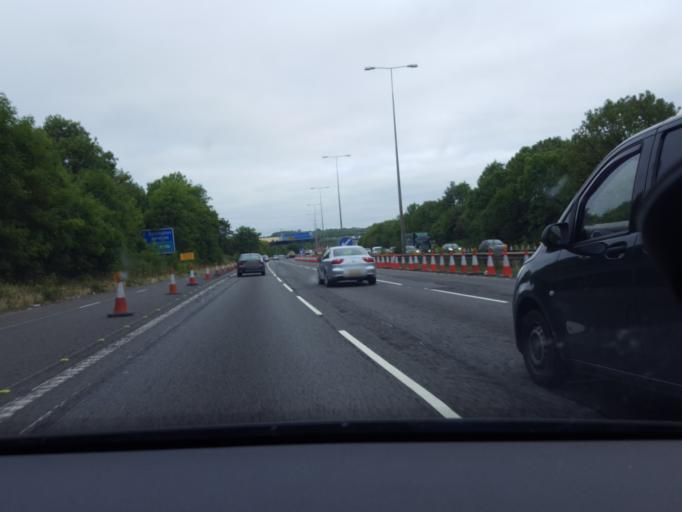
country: GB
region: England
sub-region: Leicestershire
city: Kegworth
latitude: 52.8065
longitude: -1.3046
